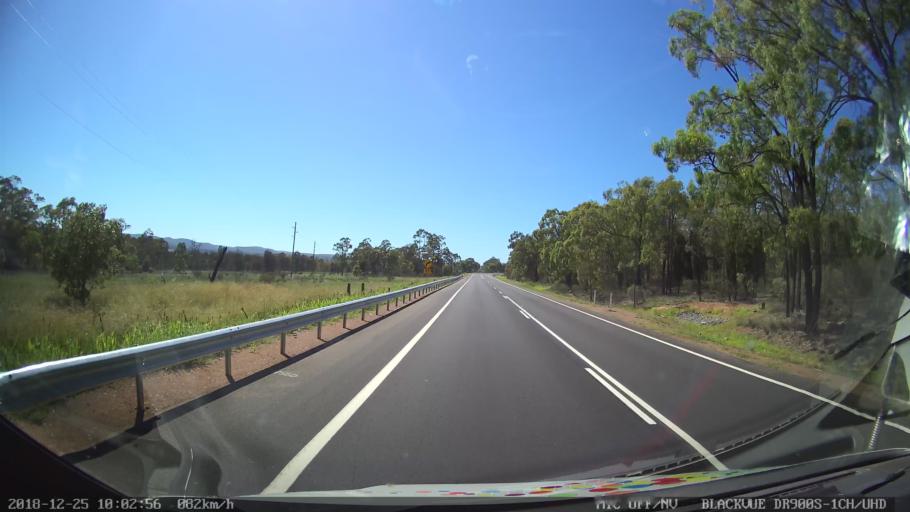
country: AU
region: New South Wales
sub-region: Upper Hunter Shire
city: Merriwa
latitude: -32.2237
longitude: 150.4668
